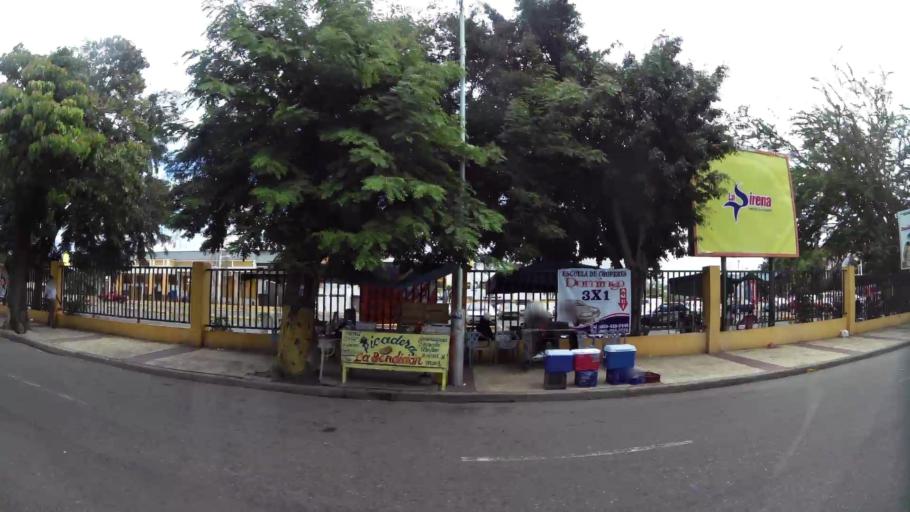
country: DO
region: Santiago
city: Santiago de los Caballeros
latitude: 19.4670
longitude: -70.7103
